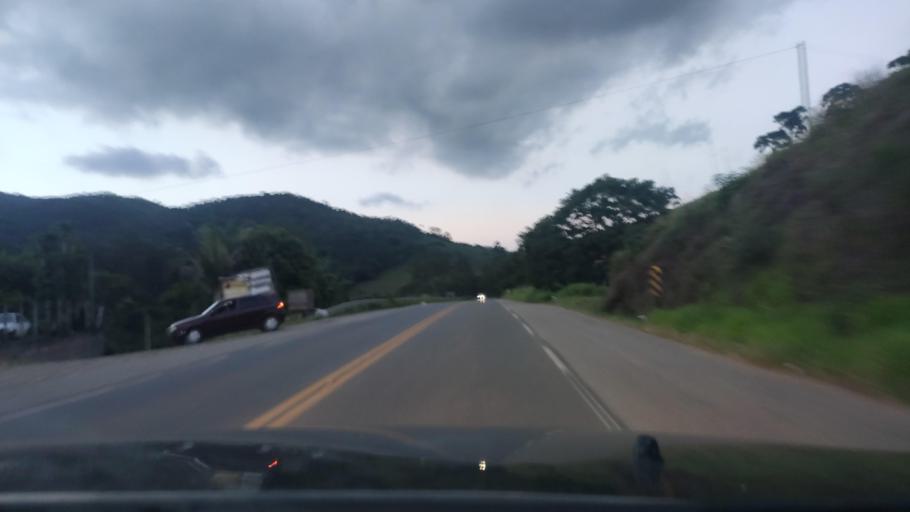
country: BR
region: Sao Paulo
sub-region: Campos Do Jordao
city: Campos do Jordao
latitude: -22.7799
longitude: -45.7430
